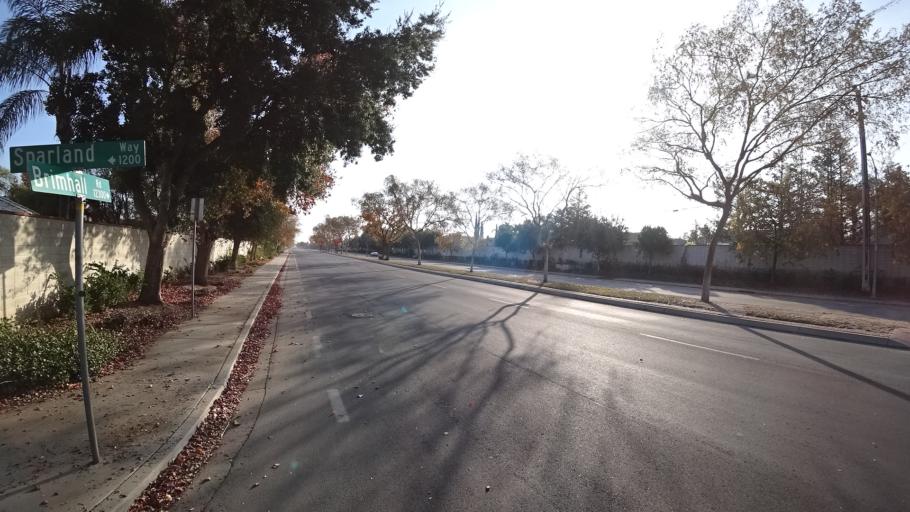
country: US
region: California
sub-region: Kern County
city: Rosedale
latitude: 35.3691
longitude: -119.1405
